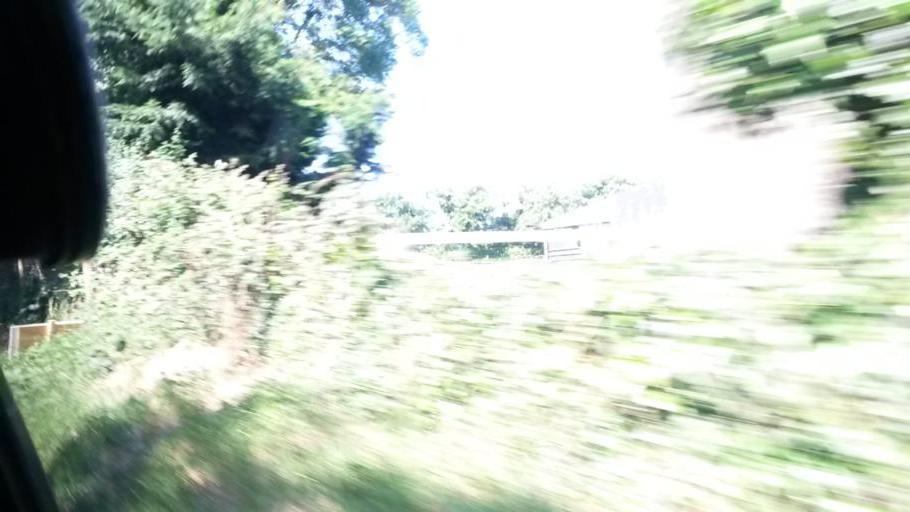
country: IE
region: Leinster
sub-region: Fingal County
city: Swords
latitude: 53.5119
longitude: -6.2678
